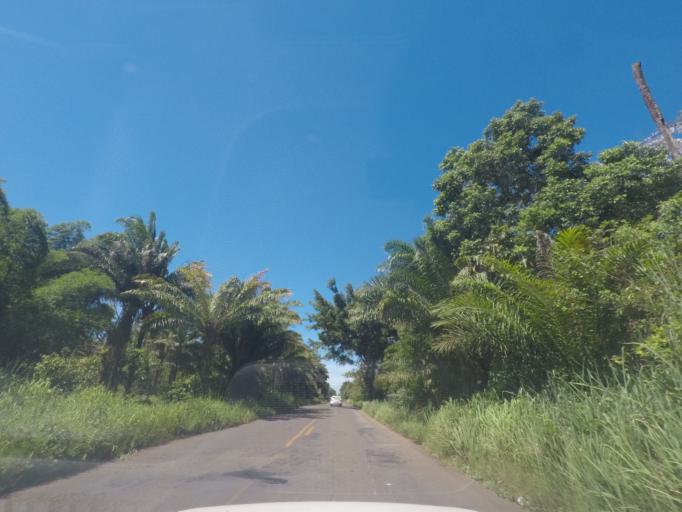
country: BR
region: Bahia
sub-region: Taperoa
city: Taperoa
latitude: -13.4933
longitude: -39.0932
